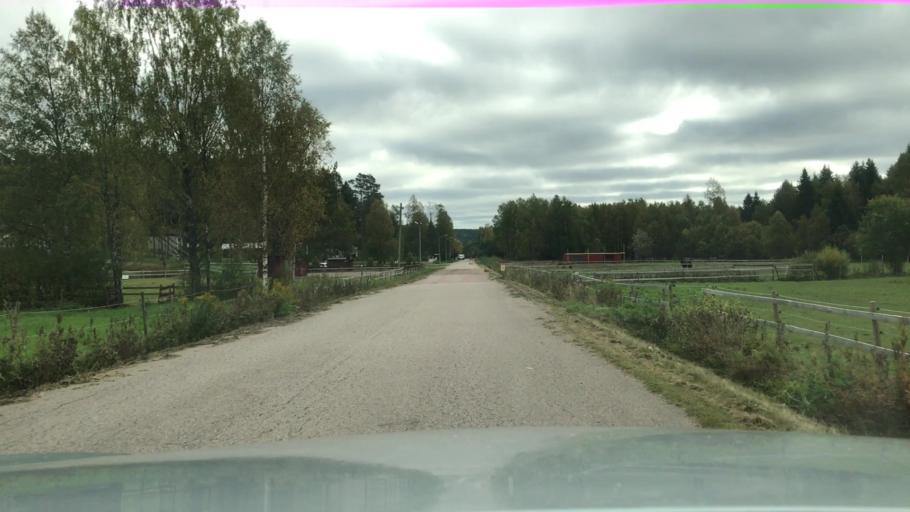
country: SE
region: Vaermland
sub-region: Munkfors Kommun
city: Munkfors
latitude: 59.8388
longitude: 13.5034
